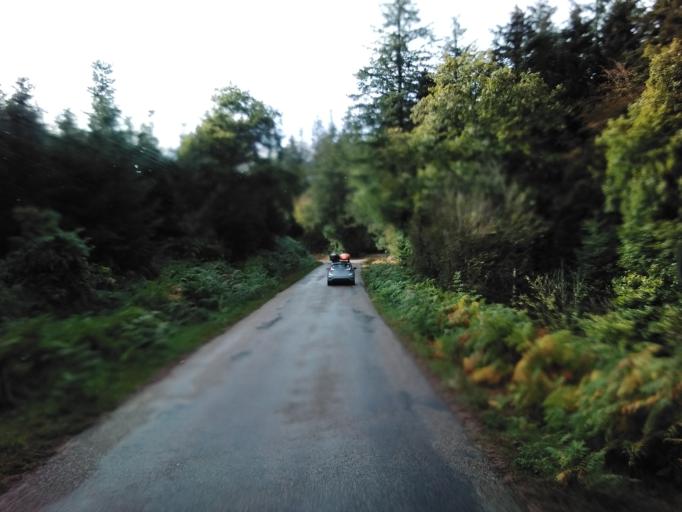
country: FR
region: Bourgogne
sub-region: Departement de la Nievre
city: Lormes
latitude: 47.2986
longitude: 3.8739
